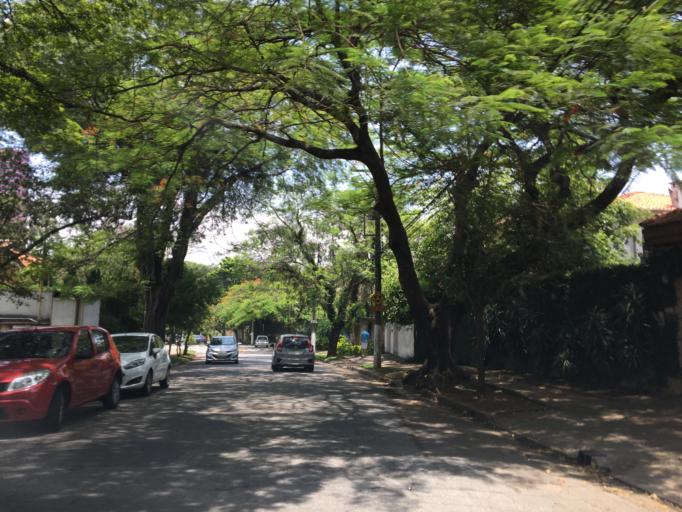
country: BR
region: Sao Paulo
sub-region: Sao Paulo
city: Sao Paulo
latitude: -23.5575
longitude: -46.6931
